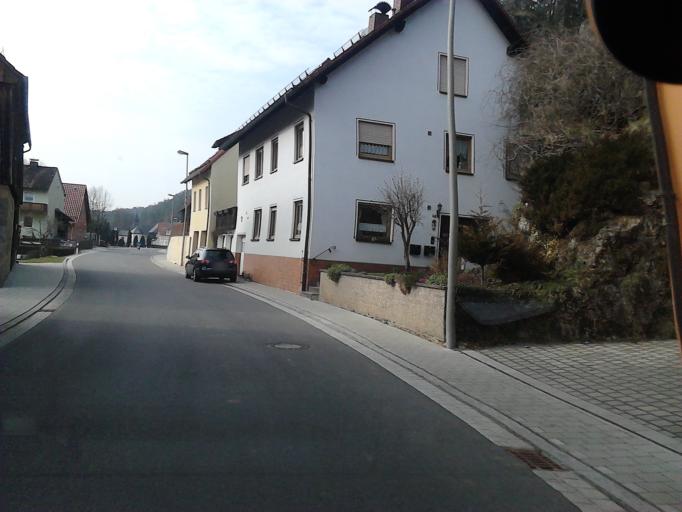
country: DE
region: Bavaria
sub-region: Upper Franconia
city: Stadelhofen
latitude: 49.9648
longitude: 11.2021
